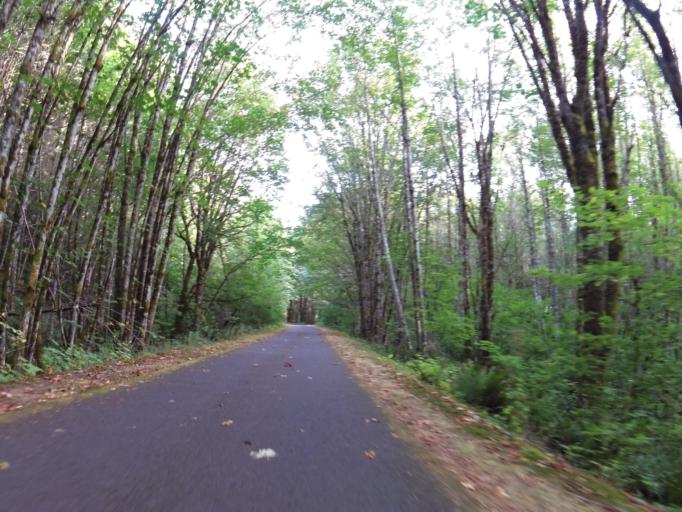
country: US
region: Washington
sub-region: Thurston County
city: Tenino
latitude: 46.9298
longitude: -122.8220
